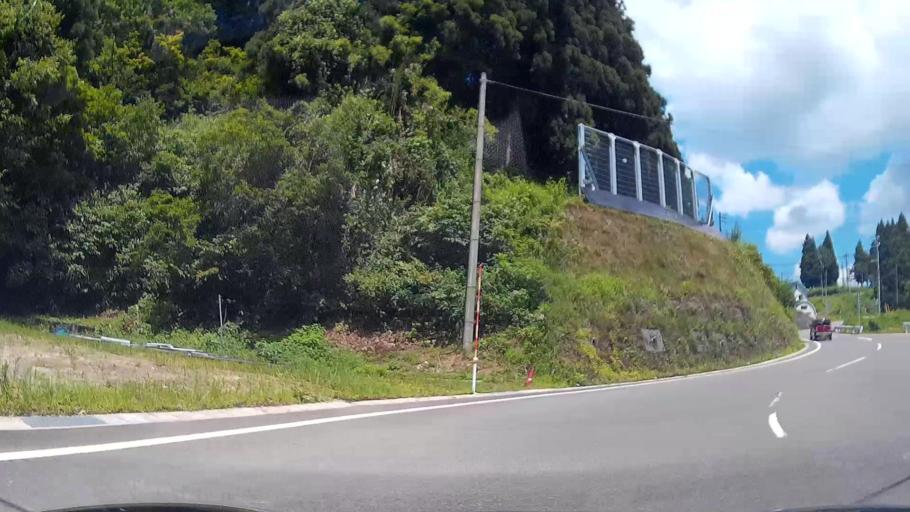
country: JP
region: Niigata
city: Shiozawa
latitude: 37.0217
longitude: 138.8017
